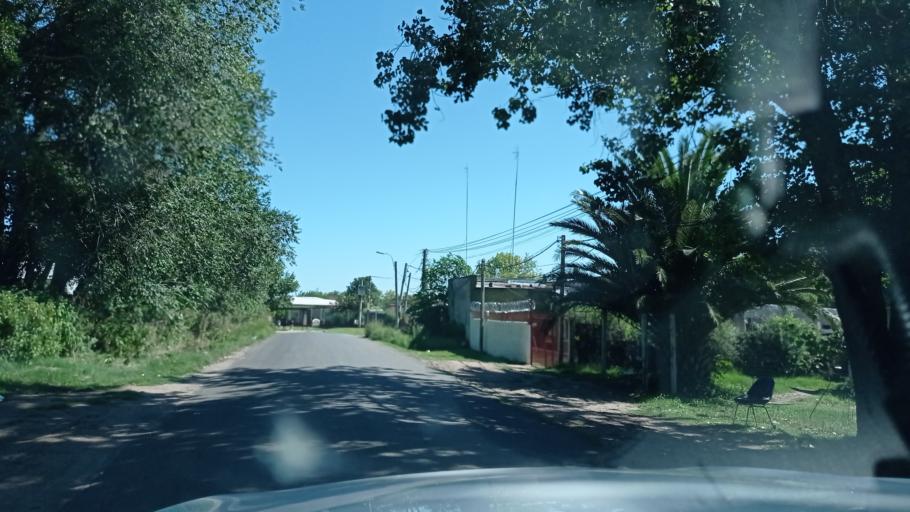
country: UY
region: Canelones
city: La Paz
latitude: -34.8317
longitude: -56.2404
